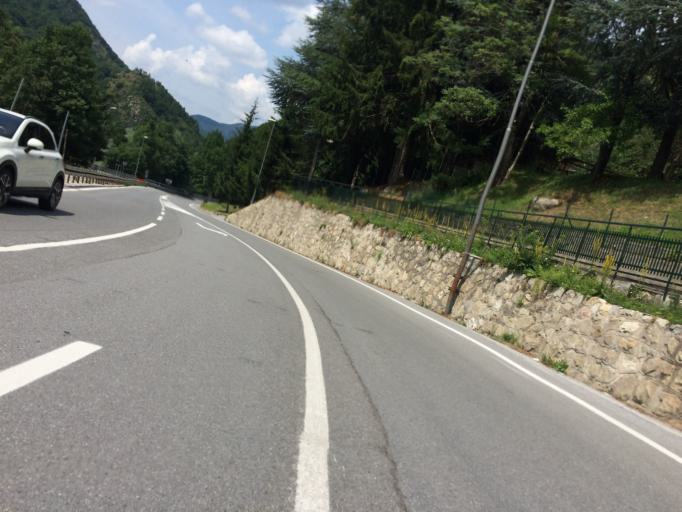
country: IT
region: Piedmont
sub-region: Provincia di Cuneo
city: Limone Piemonte
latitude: 44.2053
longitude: 7.5750
